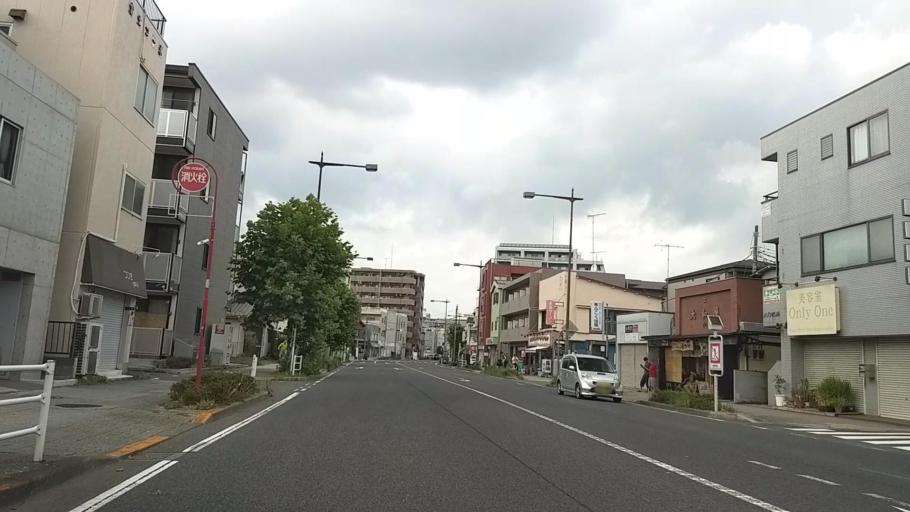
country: JP
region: Tokyo
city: Hachioji
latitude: 35.6528
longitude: 139.3331
